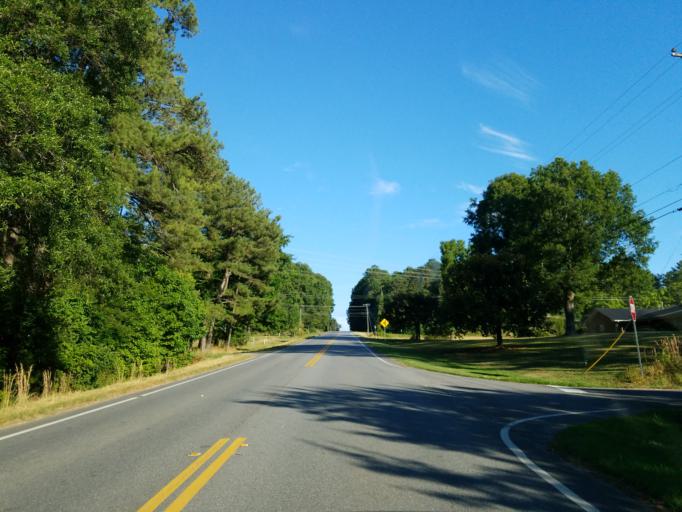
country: US
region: Georgia
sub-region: Gordon County
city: Calhoun
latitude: 34.5357
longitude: -84.9777
